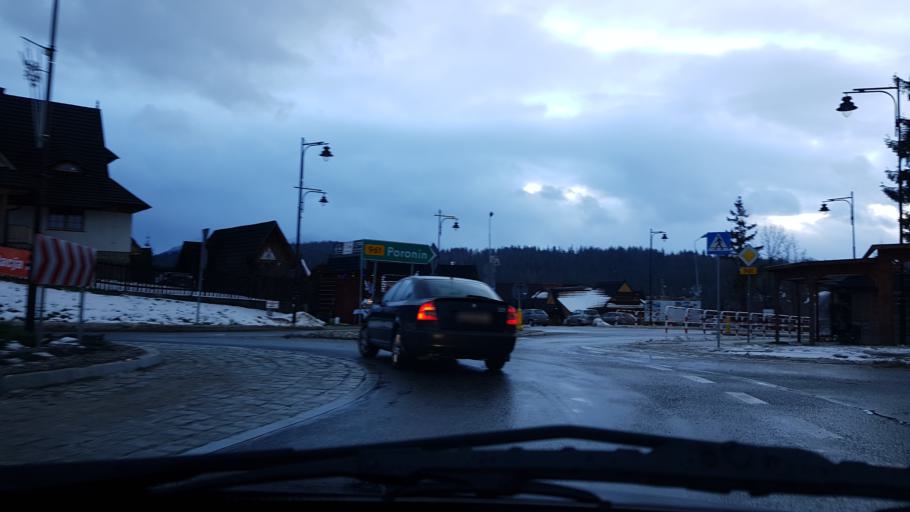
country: PL
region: Lesser Poland Voivodeship
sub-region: Powiat tatrzanski
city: Bukowina Tatrzanska
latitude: 49.3299
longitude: 20.0972
